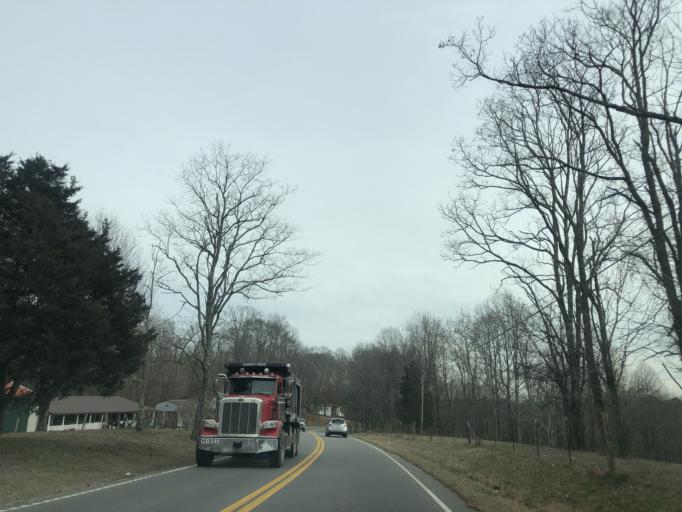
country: US
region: Tennessee
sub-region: Sumner County
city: White House
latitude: 36.4751
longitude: -86.5719
